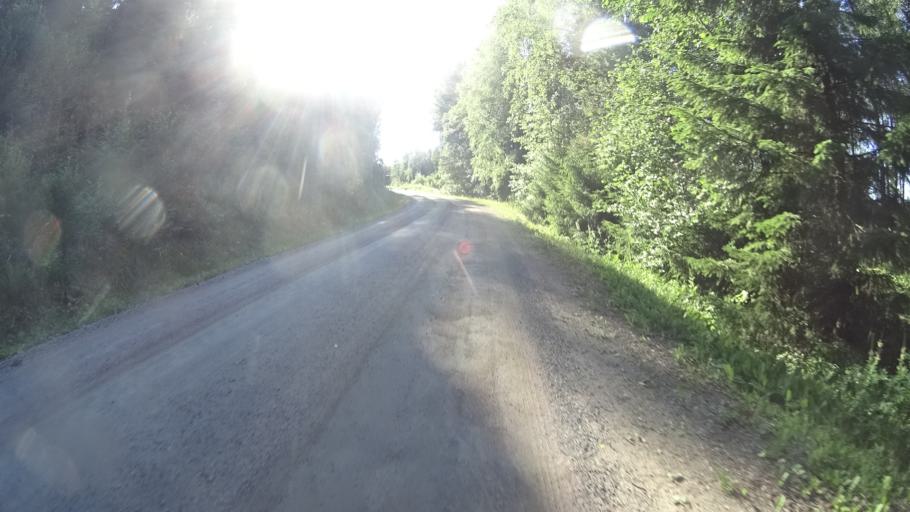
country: FI
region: Uusimaa
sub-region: Helsinki
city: Karkkila
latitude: 60.6480
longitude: 24.1513
